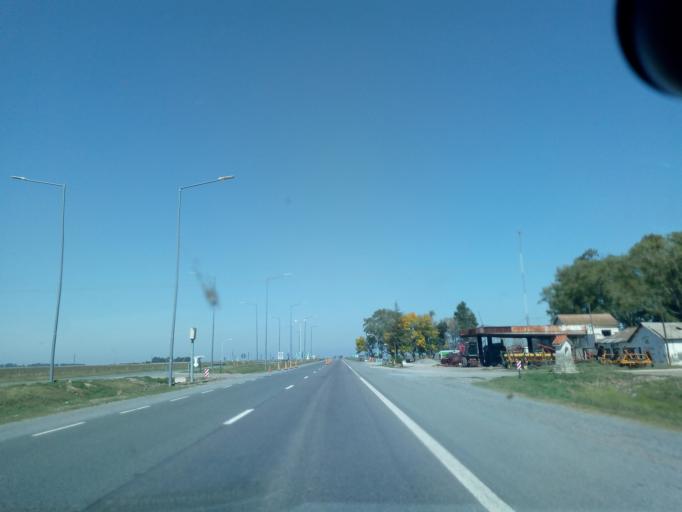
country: AR
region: Buenos Aires
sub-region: Partido de General Guido
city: General Guido
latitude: -36.6513
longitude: -57.7882
